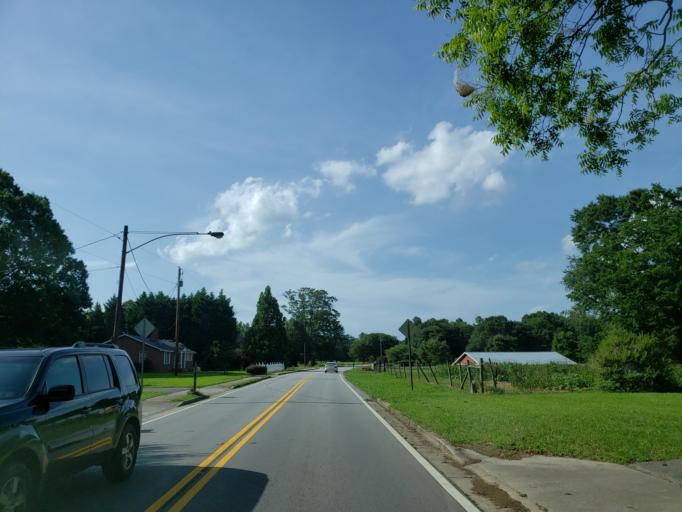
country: US
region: Georgia
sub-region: Cobb County
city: Powder Springs
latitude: 33.8967
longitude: -84.6871
